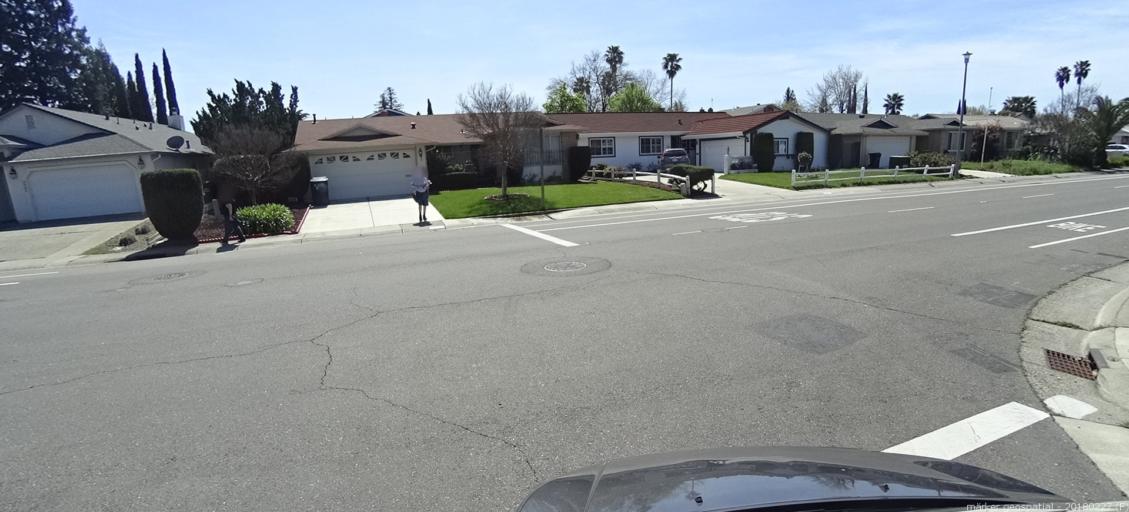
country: US
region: California
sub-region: Sacramento County
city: La Riviera
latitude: 38.5545
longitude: -121.3499
